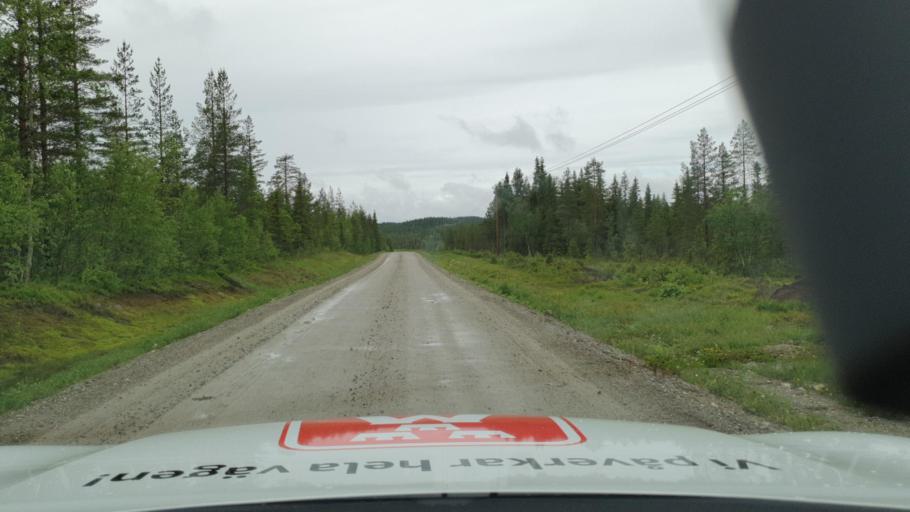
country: SE
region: Vaesterbotten
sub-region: Asele Kommun
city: Asele
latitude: 63.9683
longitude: 16.9779
